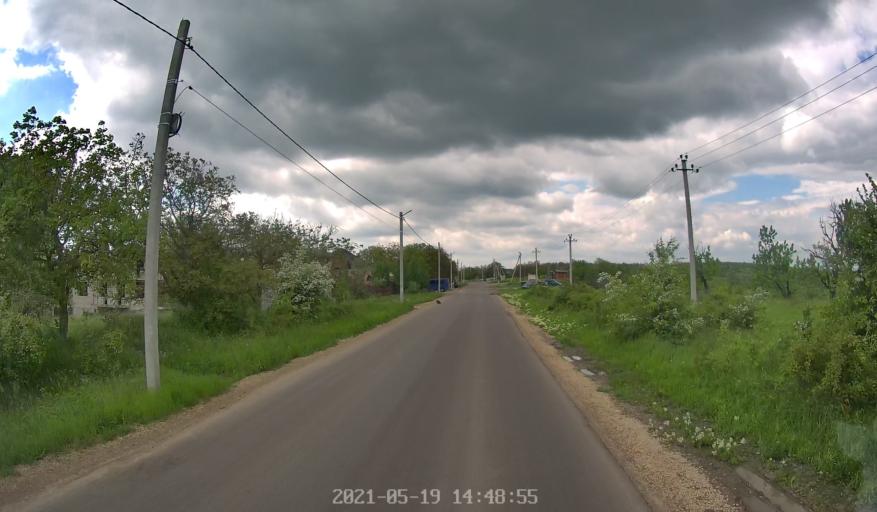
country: MD
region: Chisinau
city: Stauceni
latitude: 47.0468
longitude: 28.9563
